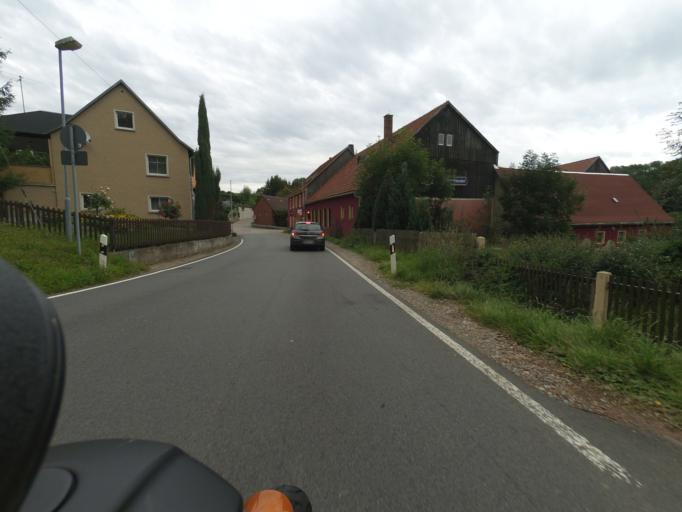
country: DE
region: Saxony
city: Reinhardtsgrimma
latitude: 50.8770
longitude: 13.7224
